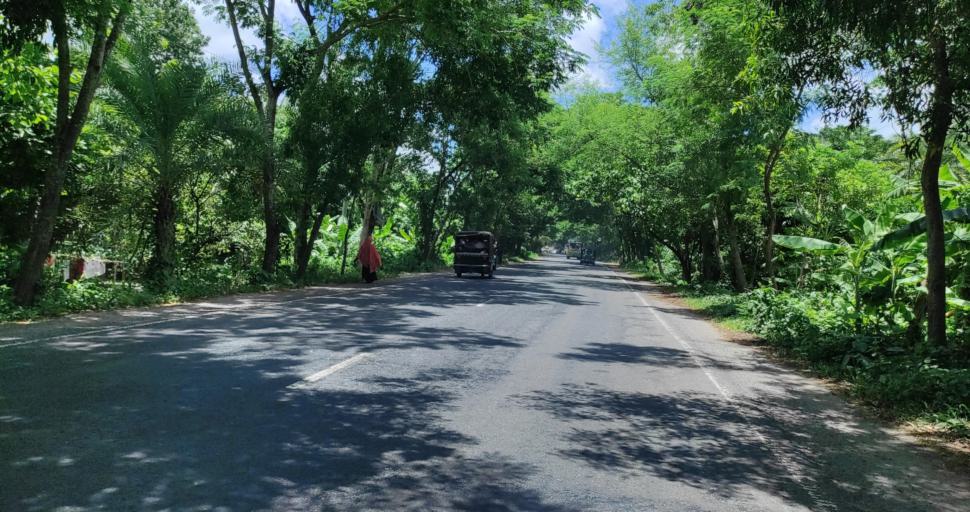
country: BD
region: Barisal
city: Gaurnadi
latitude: 22.8342
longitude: 90.2543
